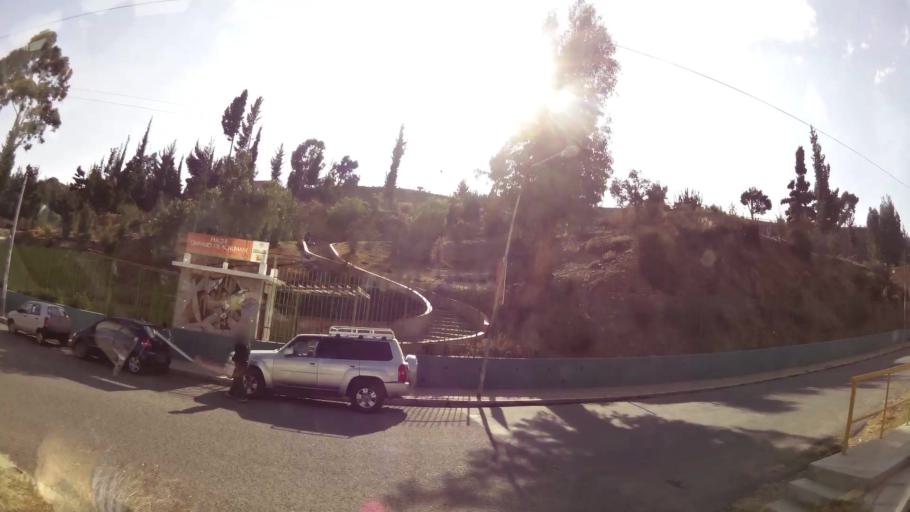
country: BO
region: La Paz
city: La Paz
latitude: -16.5290
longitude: -68.0742
